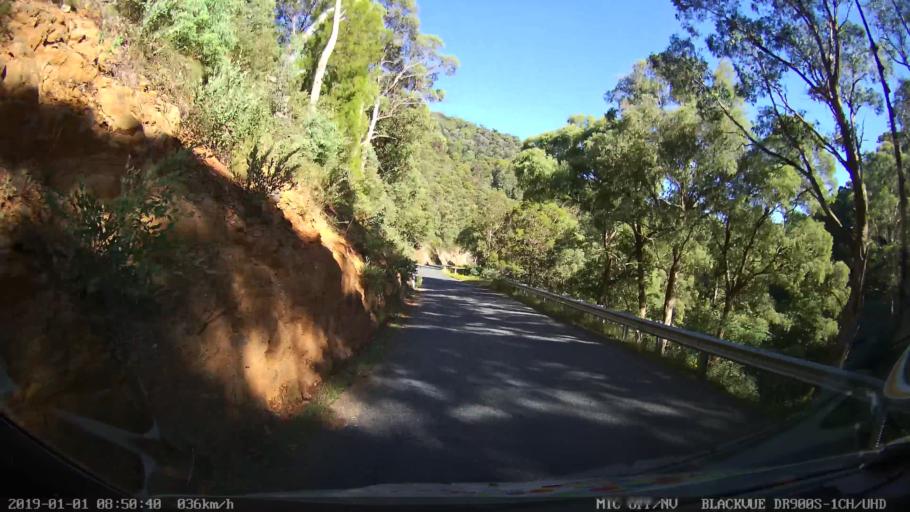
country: AU
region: New South Wales
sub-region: Snowy River
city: Jindabyne
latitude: -36.2754
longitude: 148.2020
